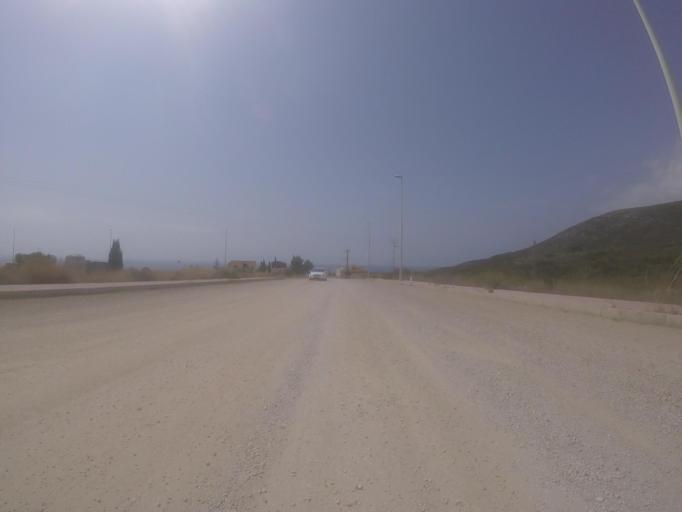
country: ES
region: Valencia
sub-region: Provincia de Castello
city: Peniscola
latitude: 40.3458
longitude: 0.3744
